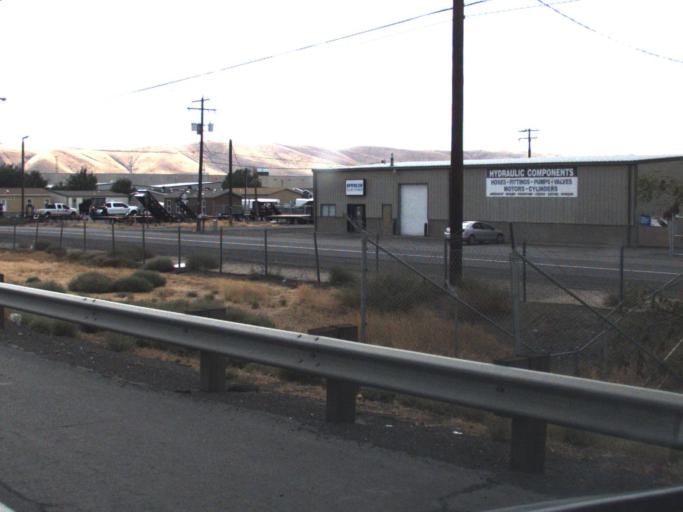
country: US
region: Washington
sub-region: Yakima County
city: Union Gap
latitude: 46.5741
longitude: -120.4720
